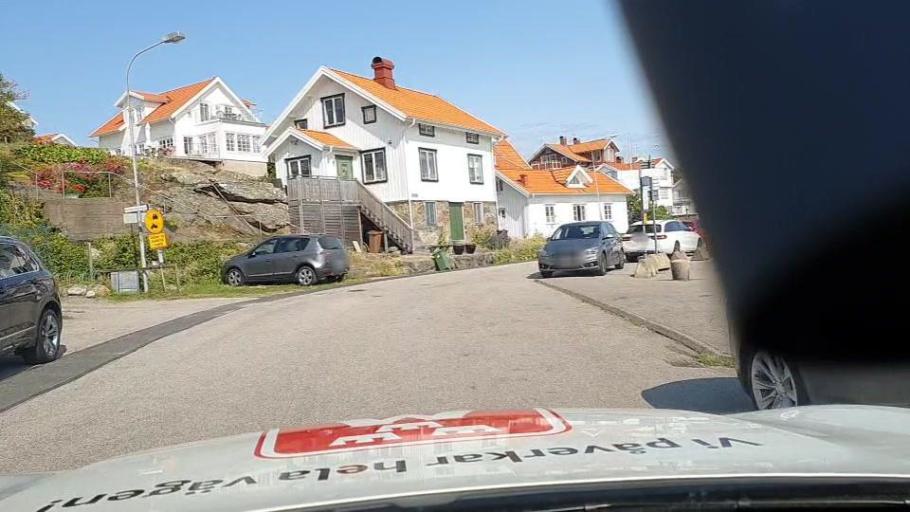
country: SE
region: Vaestra Goetaland
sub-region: Tjorns Kommun
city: Skaerhamn
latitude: 58.0740
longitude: 11.4692
